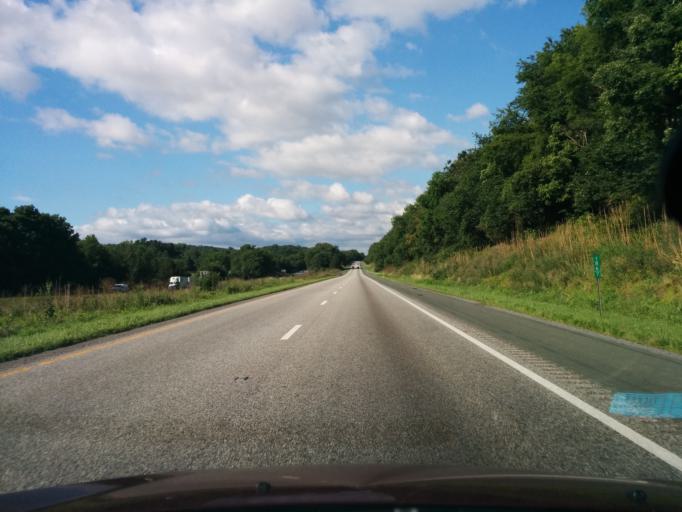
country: US
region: Virginia
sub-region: City of Lexington
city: Lexington
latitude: 37.7324
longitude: -79.4295
